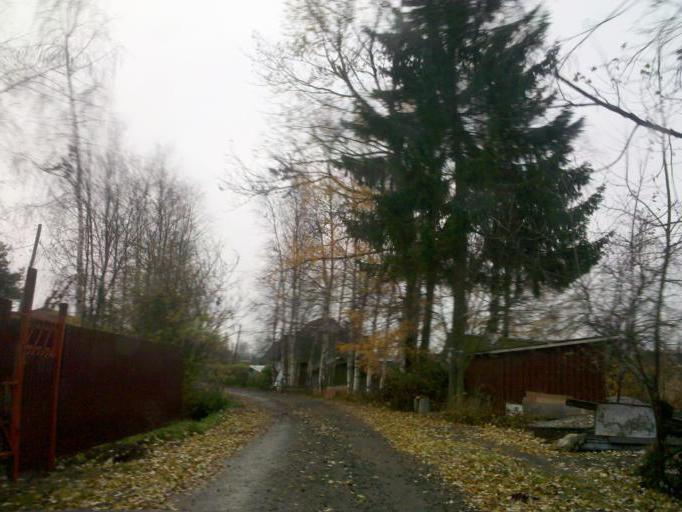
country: RU
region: Republic of Karelia
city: Shuya
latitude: 61.8535
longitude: 34.1468
